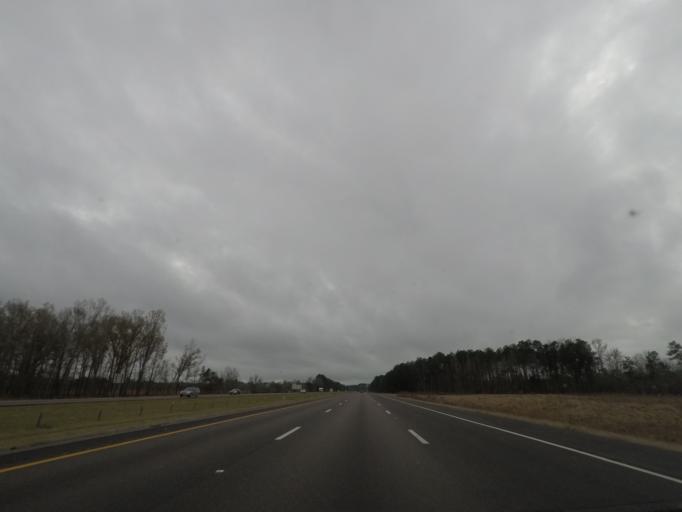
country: US
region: South Carolina
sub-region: Orangeburg County
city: Holly Hill
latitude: 33.4590
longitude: -80.4790
